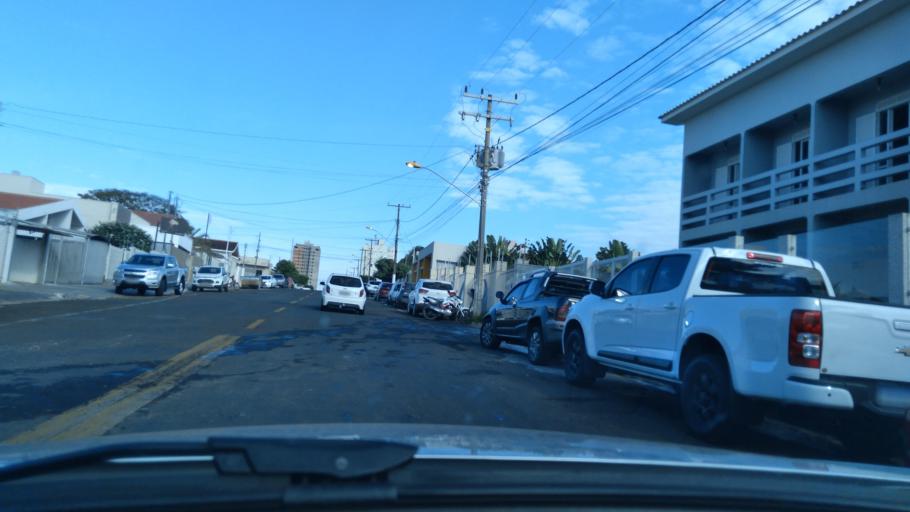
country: BR
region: Goias
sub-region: Mineiros
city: Mineiros
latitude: -17.5617
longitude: -52.5548
